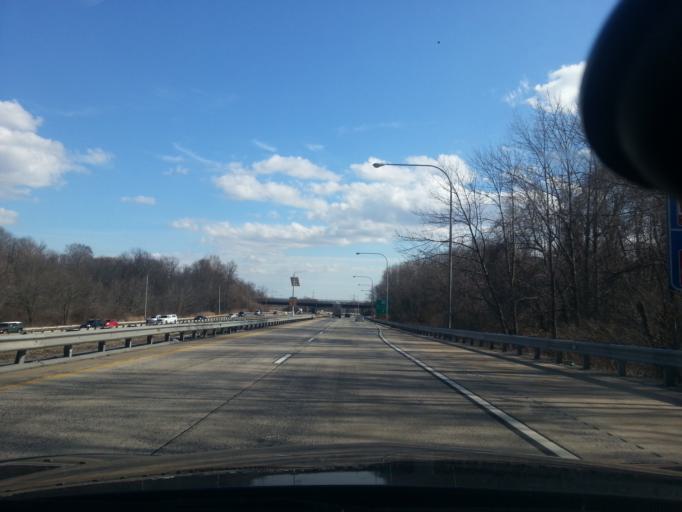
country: US
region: Delaware
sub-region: New Castle County
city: Claymont
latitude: 39.8106
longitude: -75.4548
